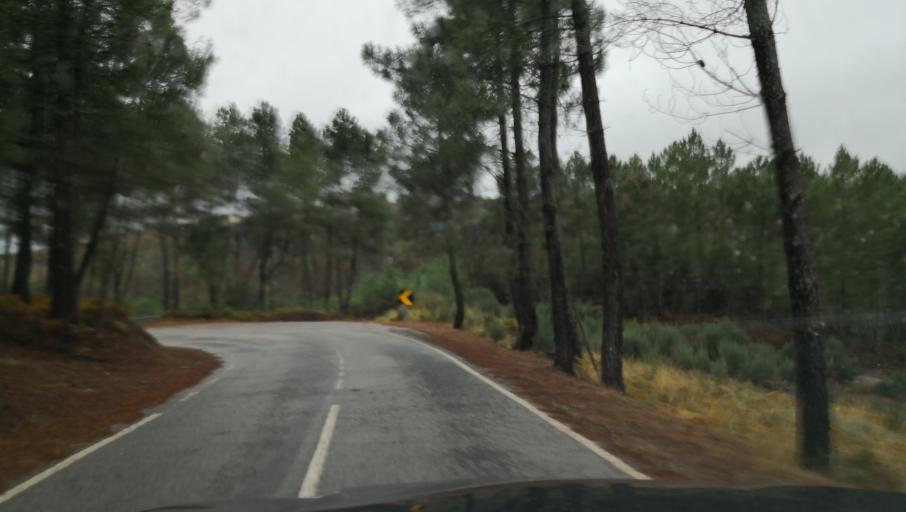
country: PT
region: Vila Real
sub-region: Sabrosa
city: Sabrosa
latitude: 41.3436
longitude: -7.5888
